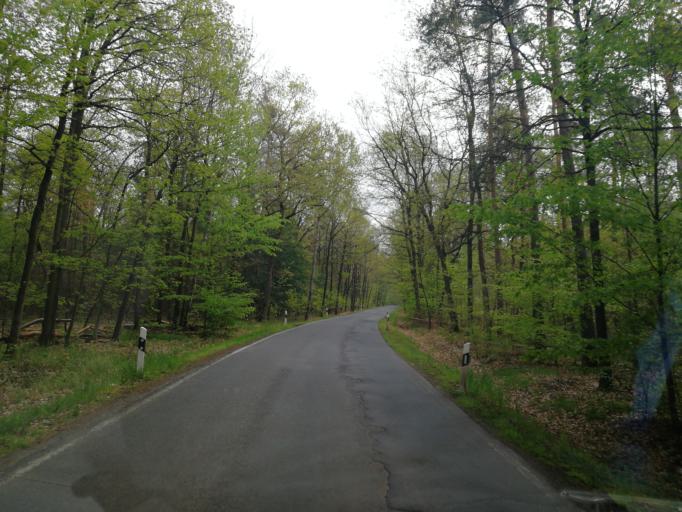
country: DE
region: Brandenburg
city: Herzberg
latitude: 51.6446
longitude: 13.1661
